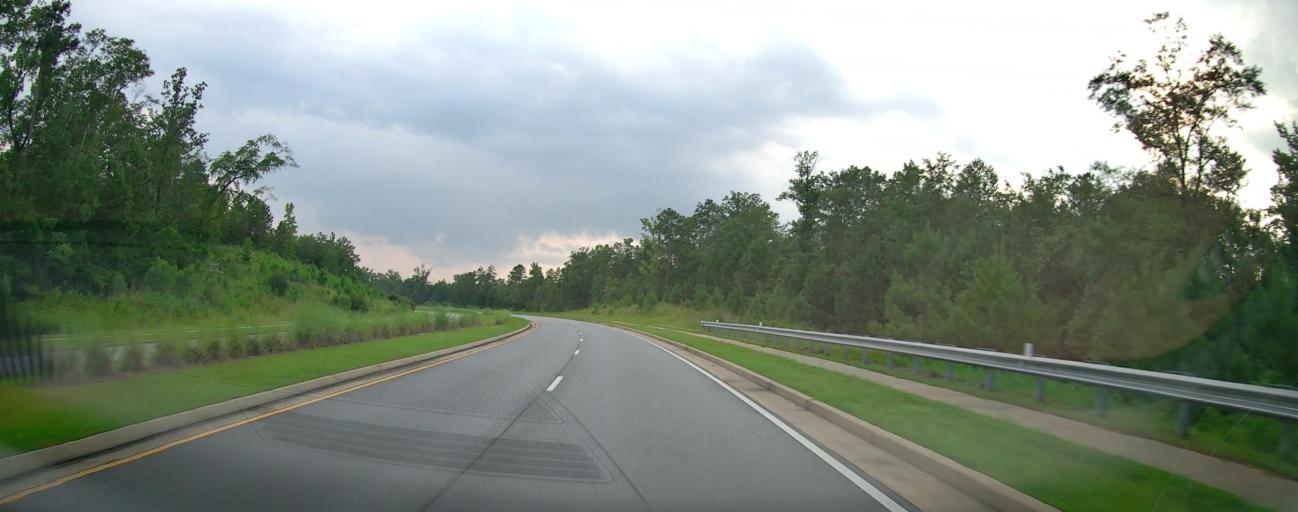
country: US
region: Georgia
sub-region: Muscogee County
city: Columbus
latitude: 32.5117
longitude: -84.8510
